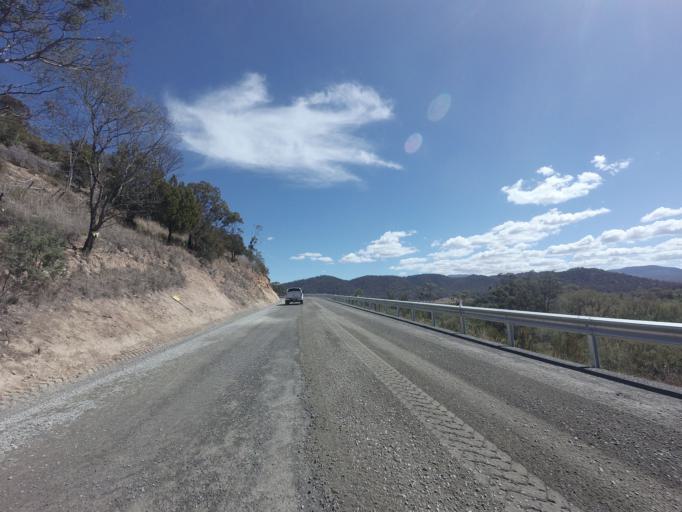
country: AU
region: Tasmania
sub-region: Break O'Day
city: St Helens
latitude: -41.6566
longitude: 147.9199
